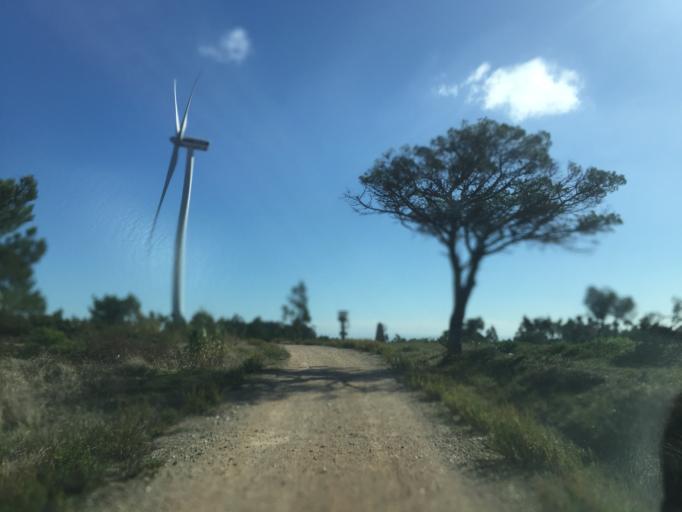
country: PT
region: Coimbra
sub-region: Figueira da Foz
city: Tavarede
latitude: 40.1964
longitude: -8.8563
